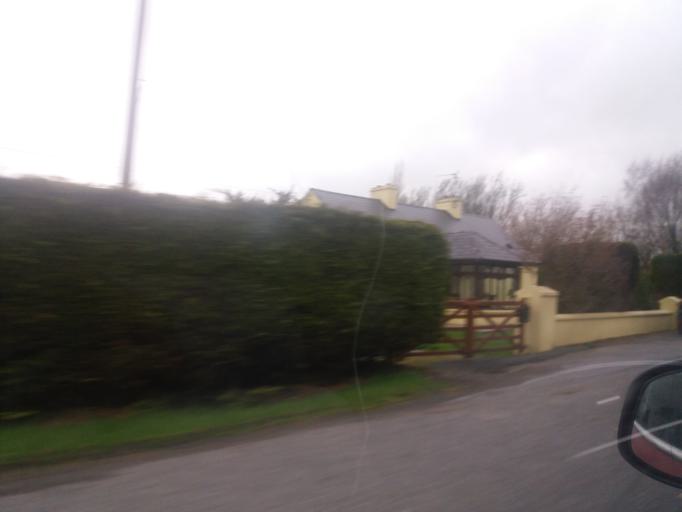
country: IE
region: Munster
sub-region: County Limerick
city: Abbeyfeale
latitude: 52.3882
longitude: -9.2782
